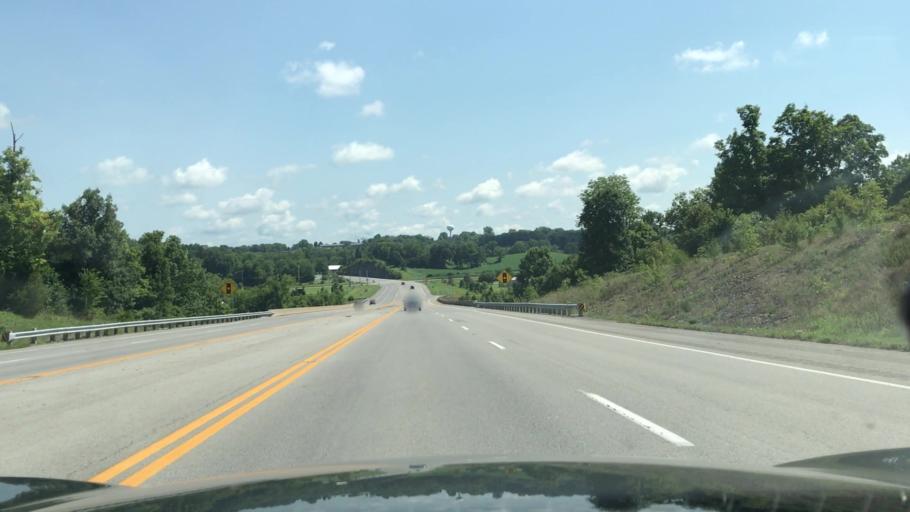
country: US
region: Kentucky
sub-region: Adair County
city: Columbia
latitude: 37.0853
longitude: -85.3251
